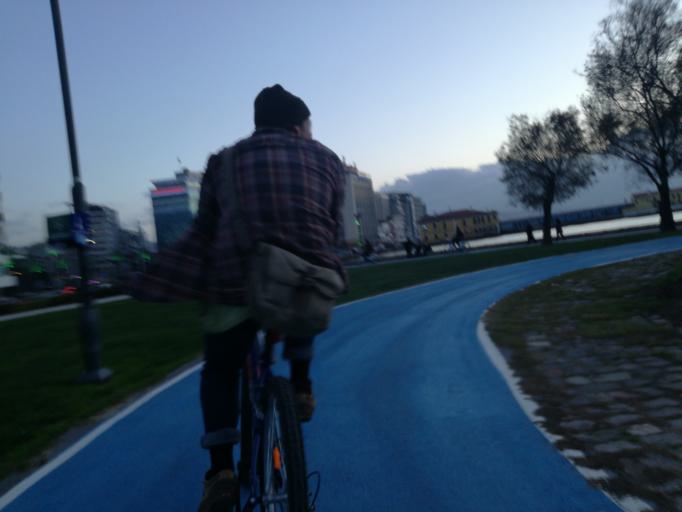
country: TR
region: Izmir
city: Izmir
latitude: 38.4305
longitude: 27.1342
